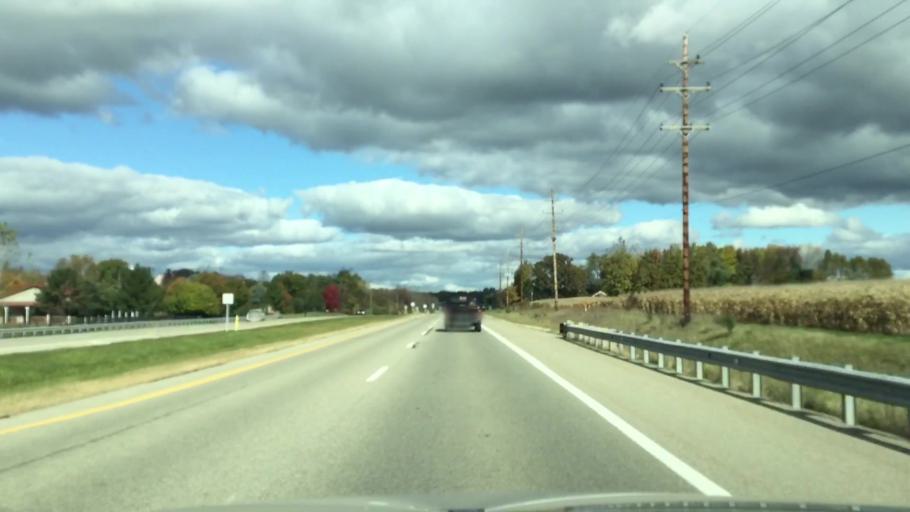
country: US
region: Michigan
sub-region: Lapeer County
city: Lapeer
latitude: 42.9805
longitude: -83.3152
